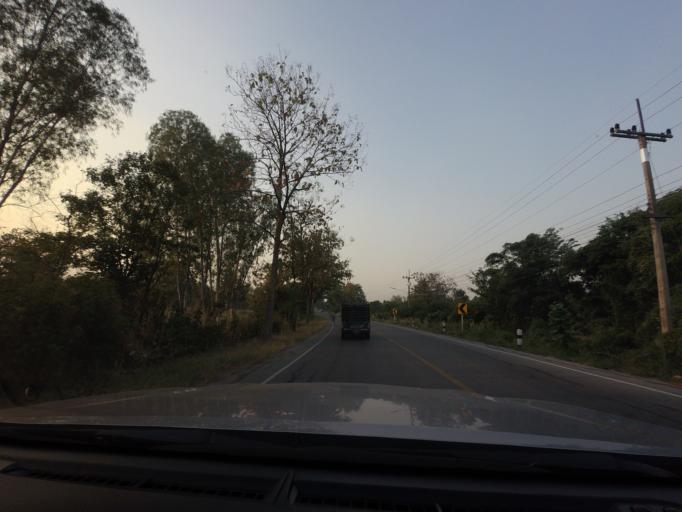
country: TH
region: Phitsanulok
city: Wang Thong
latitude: 16.7255
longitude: 100.4604
